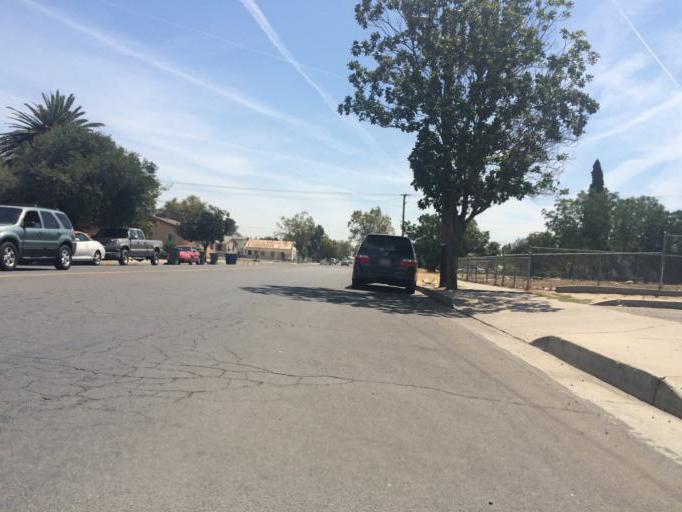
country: US
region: California
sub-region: Fresno County
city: Fresno
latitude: 36.7292
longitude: -119.8009
